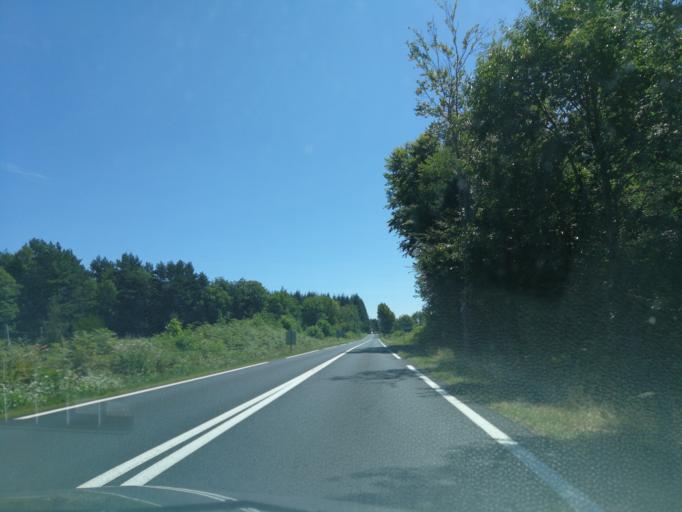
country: FR
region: Limousin
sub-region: Departement de la Correze
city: Saint-Privat
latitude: 45.0037
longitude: 2.0507
